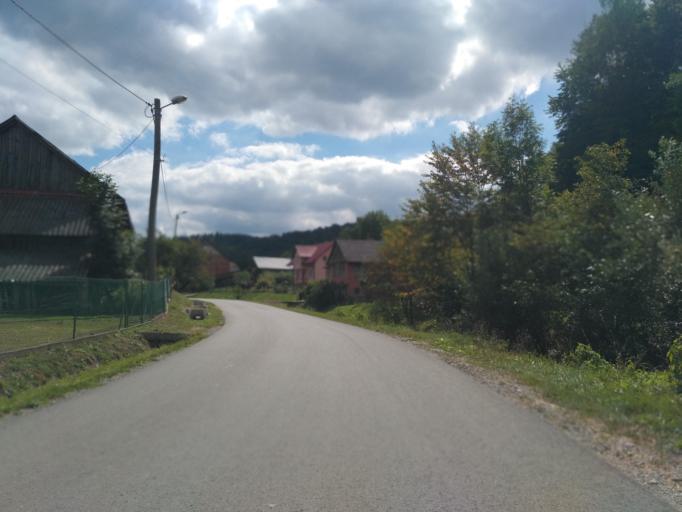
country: PL
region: Subcarpathian Voivodeship
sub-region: Powiat rzeszowski
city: Dynow
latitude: 49.7770
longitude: 22.2384
